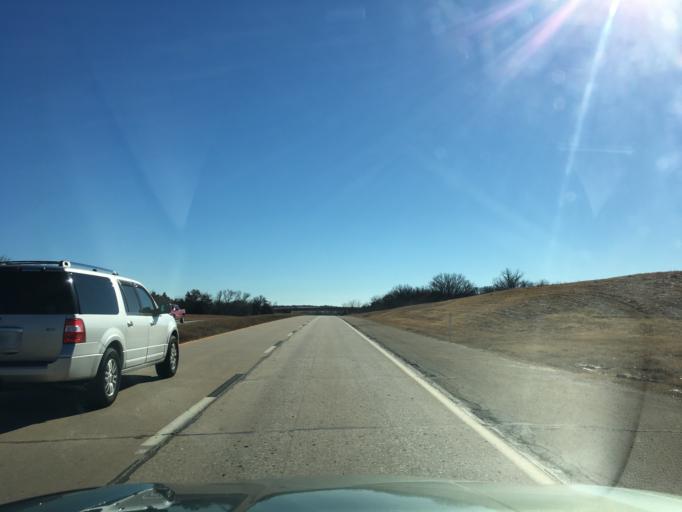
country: US
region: Oklahoma
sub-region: Payne County
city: Stillwater
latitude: 36.2654
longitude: -96.9748
